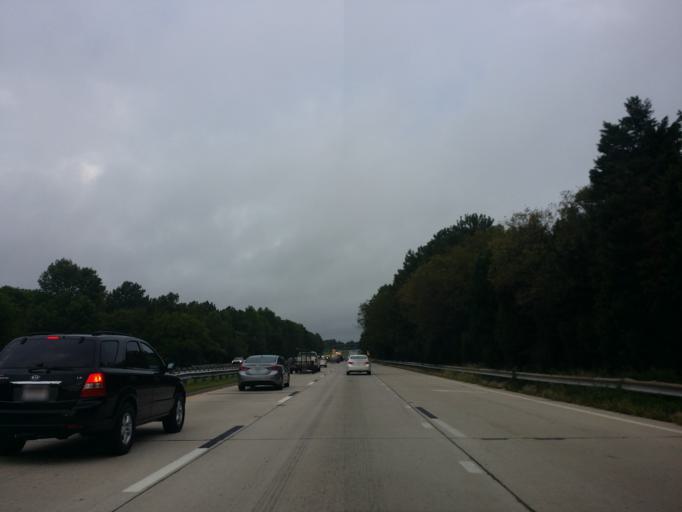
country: US
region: North Carolina
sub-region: Durham County
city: Durham
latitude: 35.9786
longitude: -78.8811
